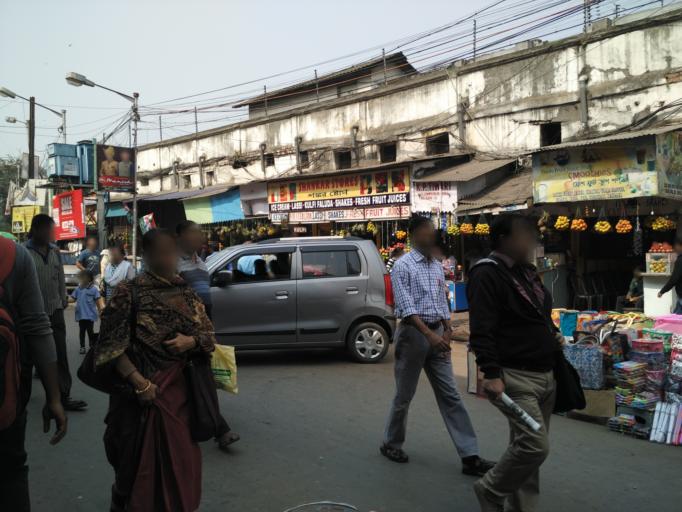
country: IN
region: West Bengal
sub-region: Kolkata
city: Bara Bazar
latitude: 22.5607
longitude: 88.3513
